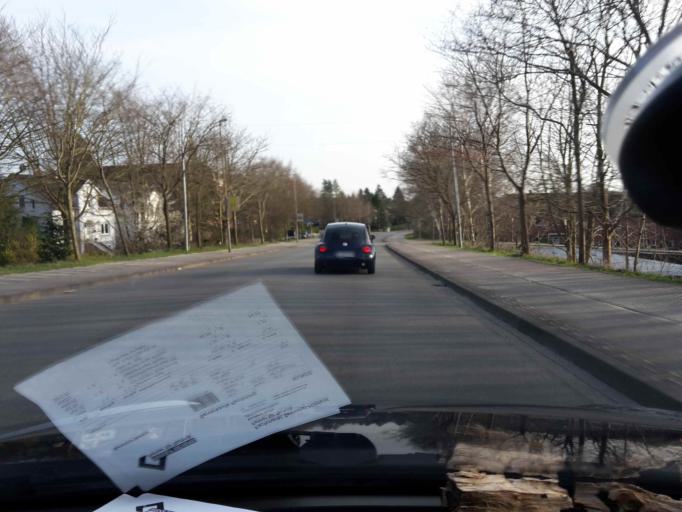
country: DE
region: Lower Saxony
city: Buchholz in der Nordheide
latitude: 53.3233
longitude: 9.8811
